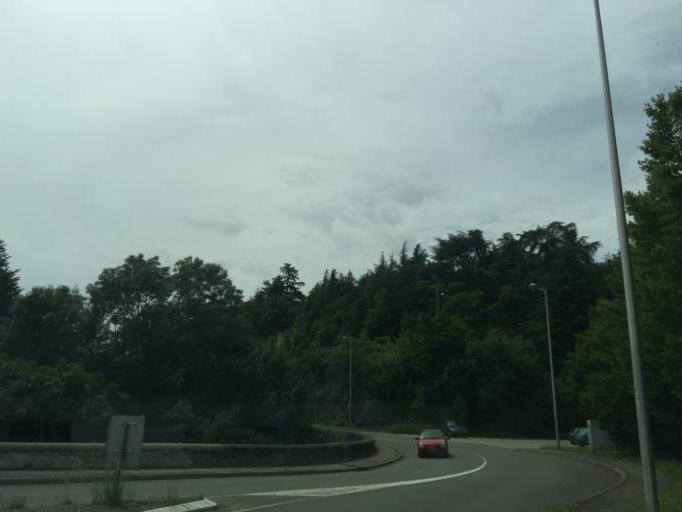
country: FR
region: Rhone-Alpes
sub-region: Departement de l'Ardeche
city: Annonay
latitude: 45.2339
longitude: 4.6726
